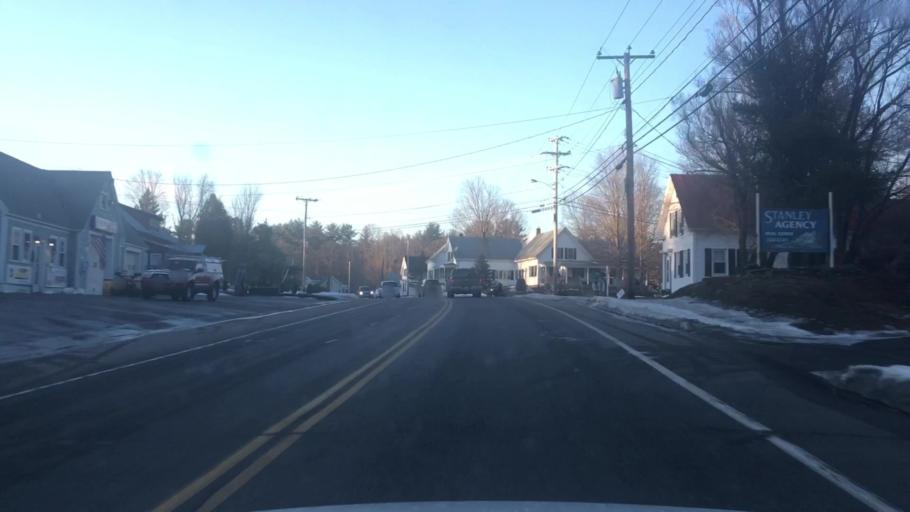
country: US
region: Maine
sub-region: York County
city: Springvale
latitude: 43.4754
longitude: -70.8113
